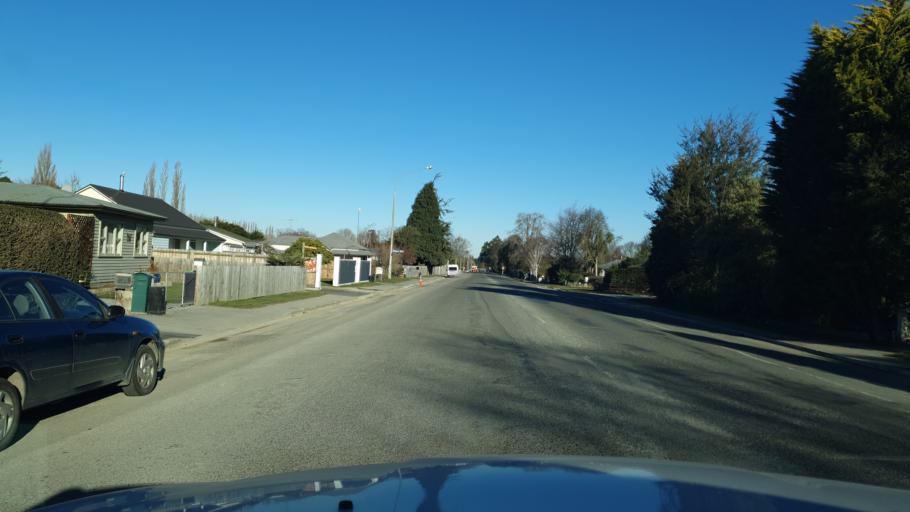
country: NZ
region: Canterbury
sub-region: Timaru District
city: Pleasant Point
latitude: -44.1067
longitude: 171.2450
